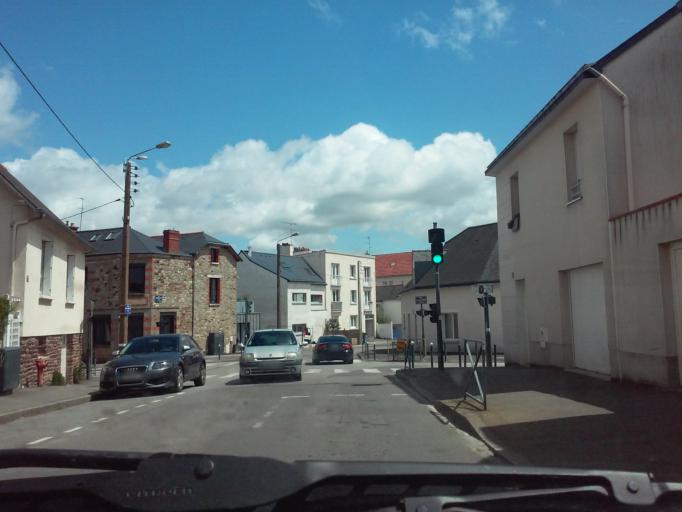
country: FR
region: Brittany
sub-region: Departement d'Ille-et-Vilaine
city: Rennes
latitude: 48.0980
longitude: -1.6613
